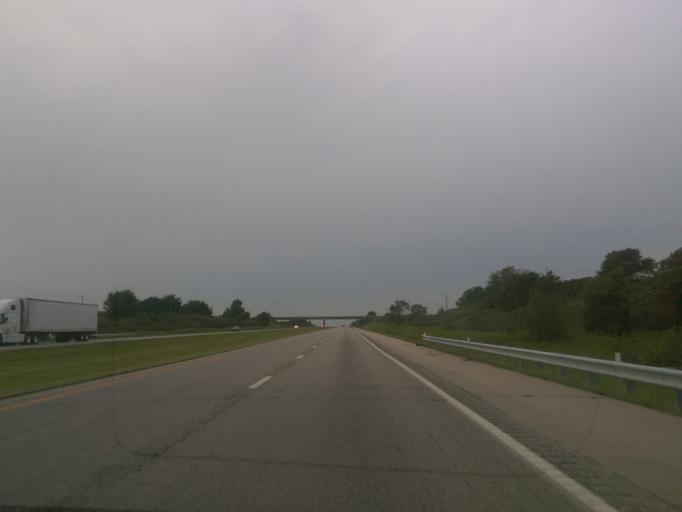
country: US
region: Missouri
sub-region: Holt County
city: Oregon
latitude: 40.0246
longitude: -95.1015
